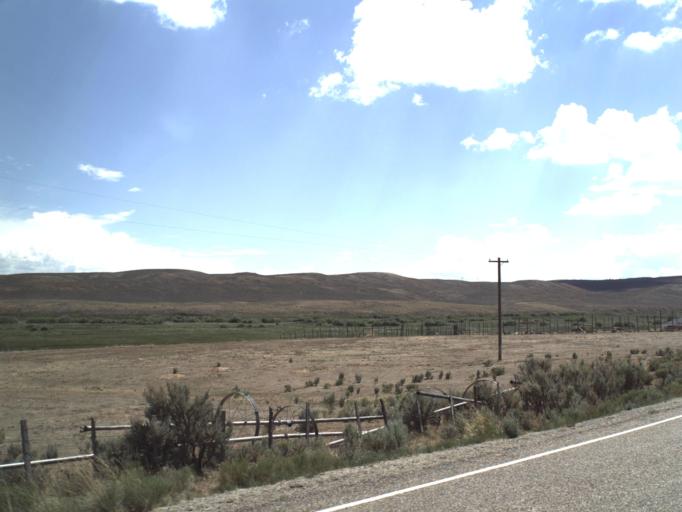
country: US
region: Utah
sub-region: Rich County
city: Randolph
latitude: 41.5181
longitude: -111.2077
